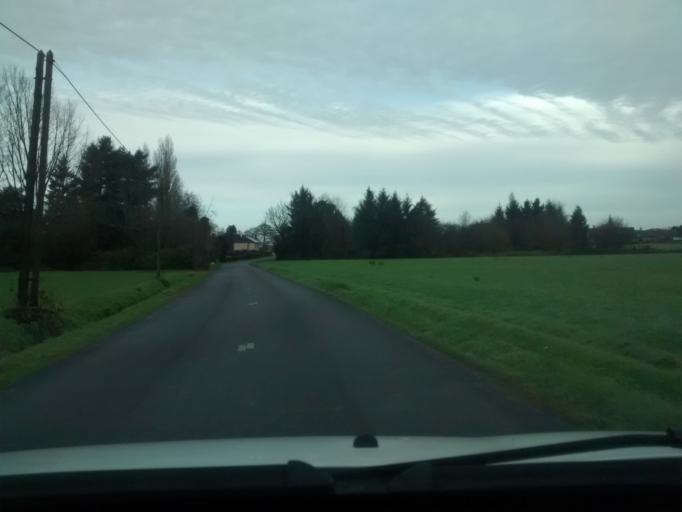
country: FR
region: Brittany
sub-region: Departement d'Ille-et-Vilaine
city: Montgermont
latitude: 48.1349
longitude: -1.7129
